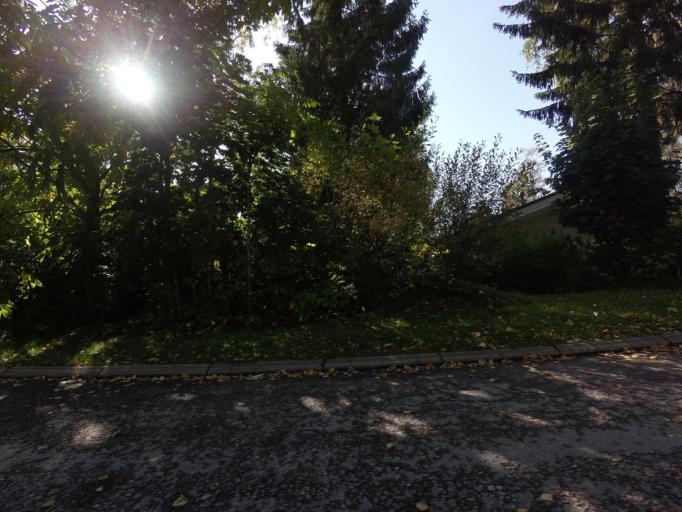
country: FI
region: Uusimaa
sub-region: Helsinki
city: Espoo
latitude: 60.1812
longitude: 24.6659
